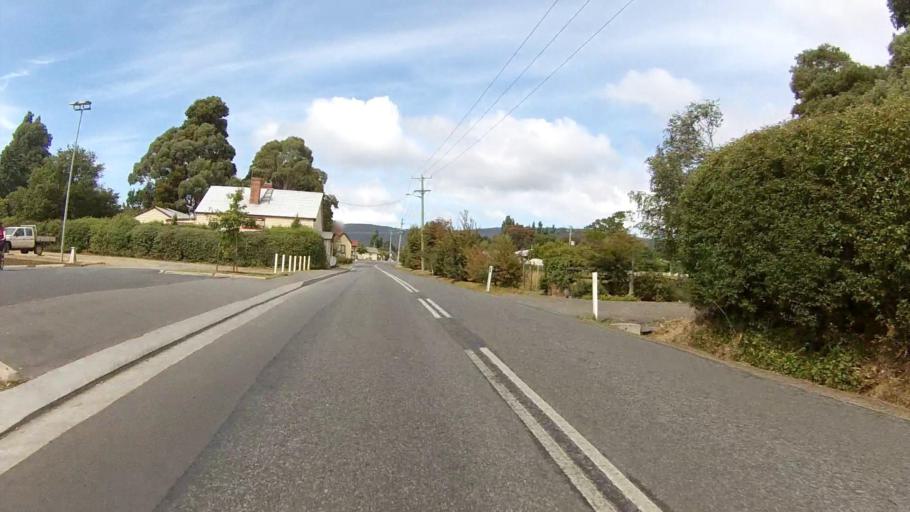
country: AU
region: Tasmania
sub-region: Kingborough
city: Kettering
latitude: -43.1585
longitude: 147.2395
